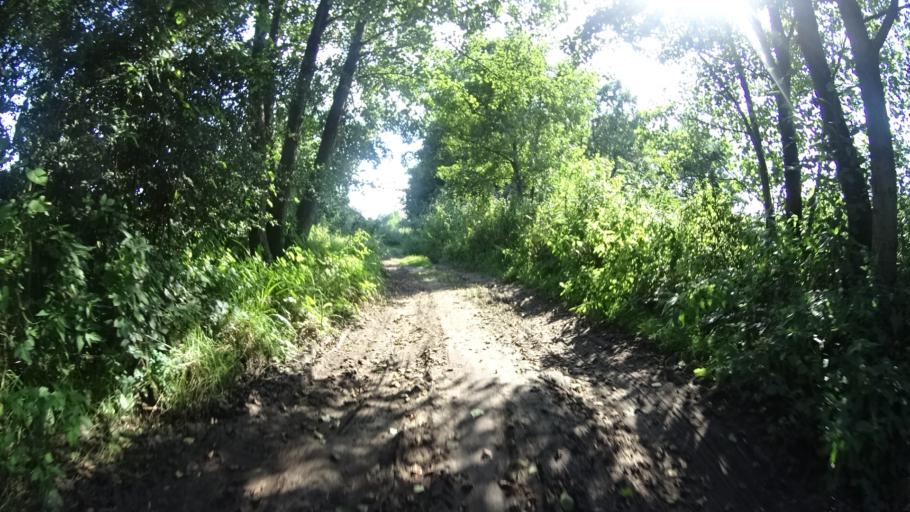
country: PL
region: Masovian Voivodeship
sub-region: Powiat bialobrzeski
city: Wysmierzyce
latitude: 51.6387
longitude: 20.8184
